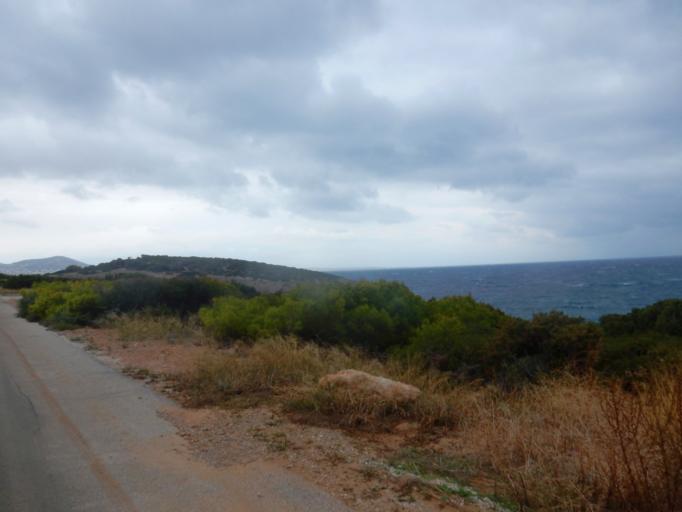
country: GR
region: Attica
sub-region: Nomarchia Anatolikis Attikis
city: Limin Mesoyaias
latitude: 37.9173
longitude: 24.0324
